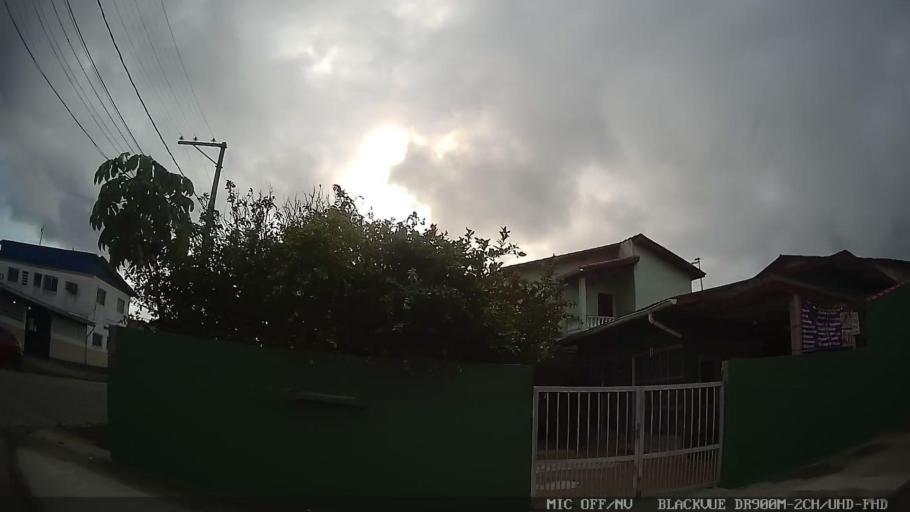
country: BR
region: Sao Paulo
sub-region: Itanhaem
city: Itanhaem
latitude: -24.1930
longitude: -46.8144
